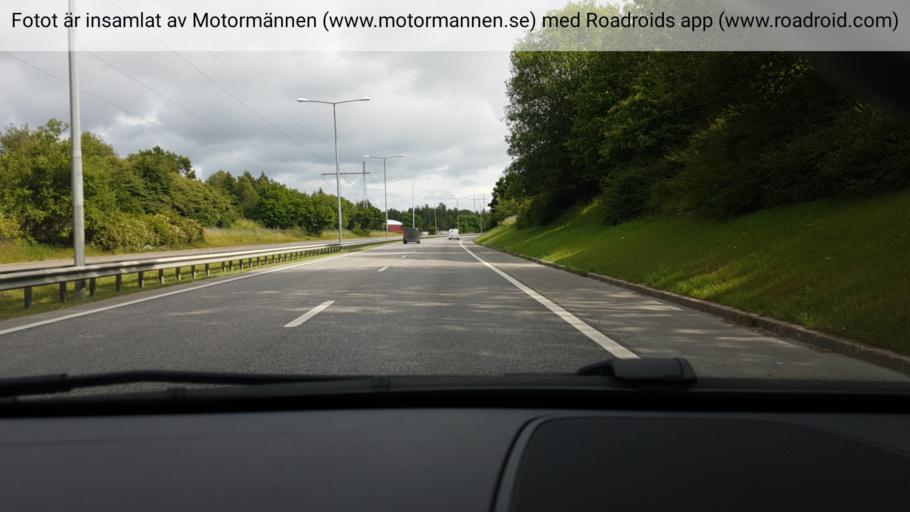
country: SE
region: Stockholm
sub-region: Stockholms Kommun
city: Arsta
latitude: 59.2670
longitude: 18.0596
